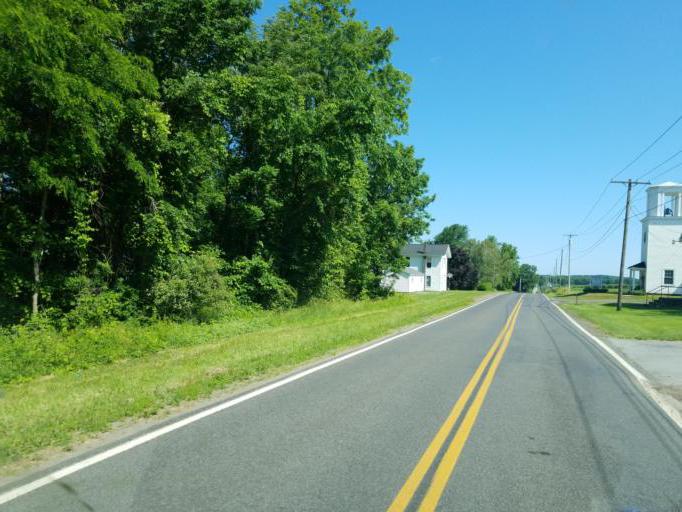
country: US
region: New York
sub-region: Wayne County
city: Wolcott
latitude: 43.2328
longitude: -76.8798
